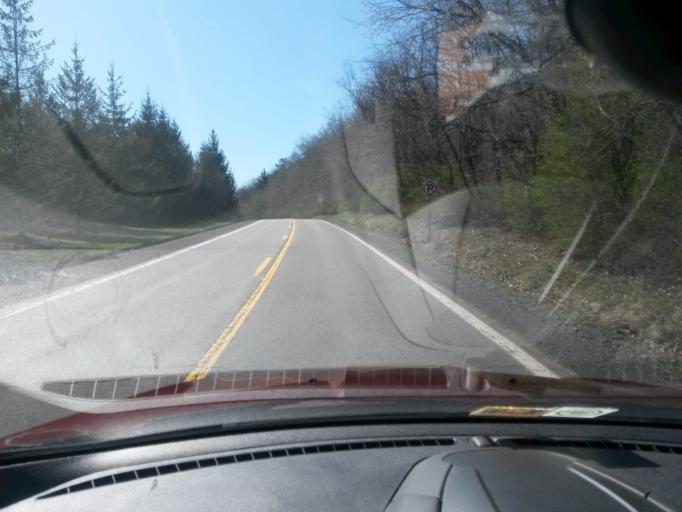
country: US
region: West Virginia
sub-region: Greenbrier County
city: White Sulphur Springs
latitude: 37.7770
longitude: -80.3422
